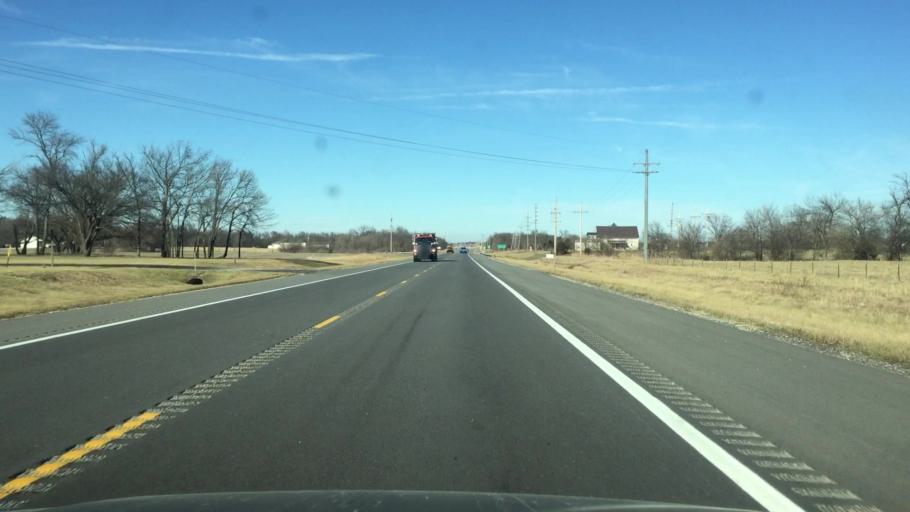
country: US
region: Kansas
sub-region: Franklin County
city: Ottawa
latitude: 38.5473
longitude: -95.2678
